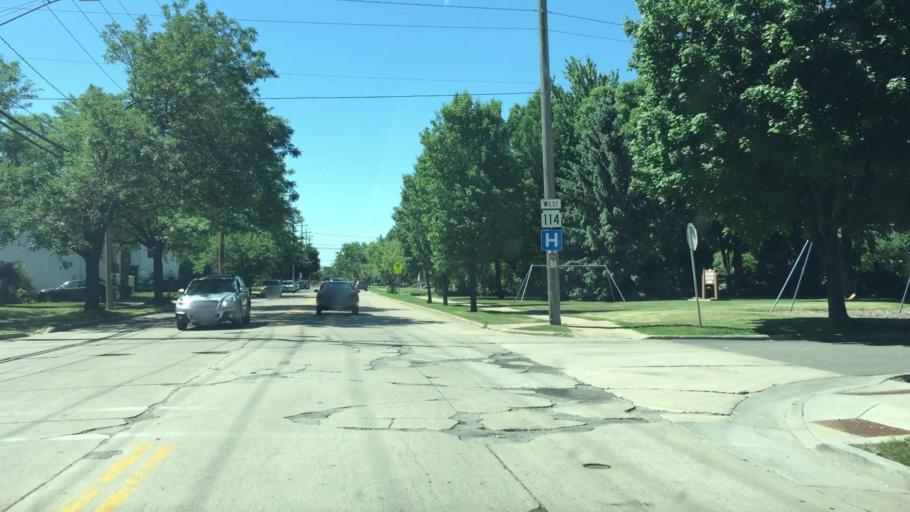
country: US
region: Wisconsin
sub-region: Winnebago County
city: Menasha
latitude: 44.2040
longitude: -88.4532
